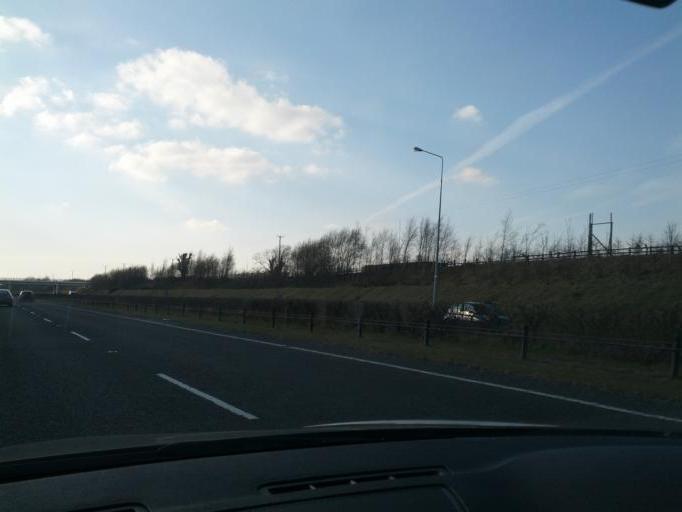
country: IE
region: Leinster
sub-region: Kildare
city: Kildare
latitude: 53.1533
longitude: -6.9297
